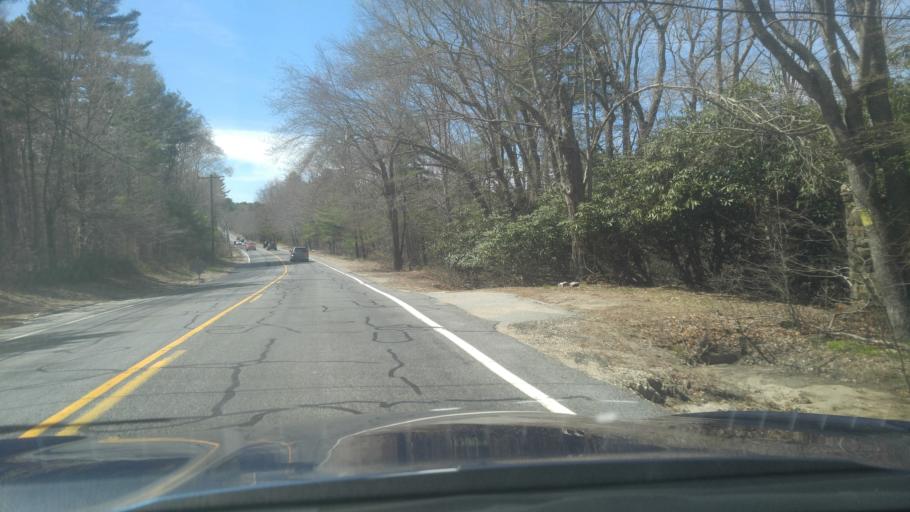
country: US
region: Rhode Island
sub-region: Kent County
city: West Greenwich
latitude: 41.5884
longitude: -71.6234
